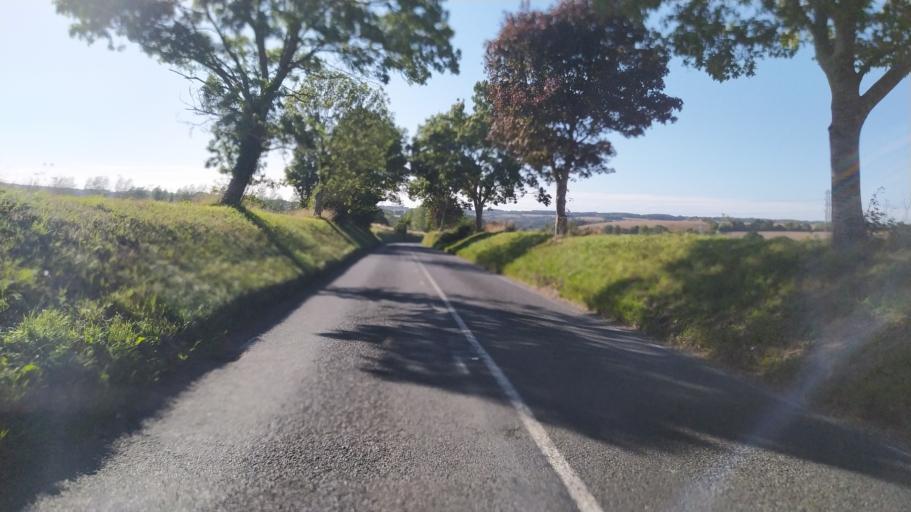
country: GB
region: England
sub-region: Hampshire
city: Alton
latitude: 51.1382
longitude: -0.9393
